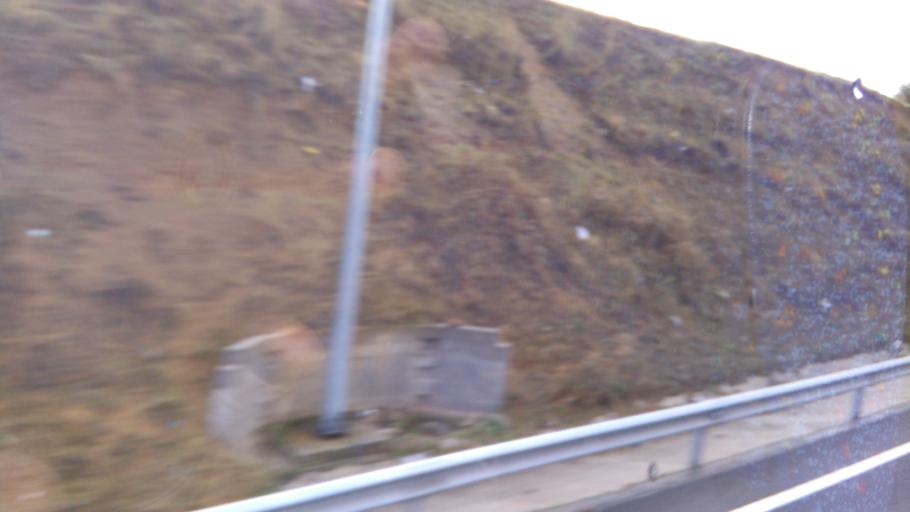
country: ES
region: Madrid
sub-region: Provincia de Madrid
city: Latina
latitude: 40.3627
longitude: -3.7432
